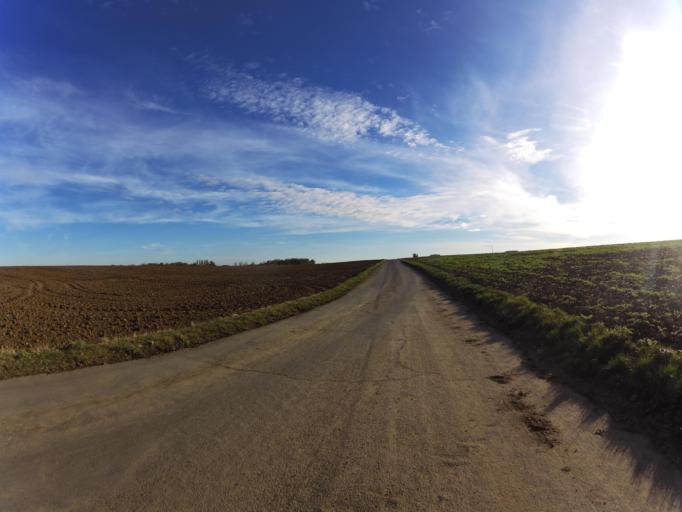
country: DE
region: Bavaria
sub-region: Regierungsbezirk Unterfranken
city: Giebelstadt
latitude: 49.6627
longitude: 9.9579
